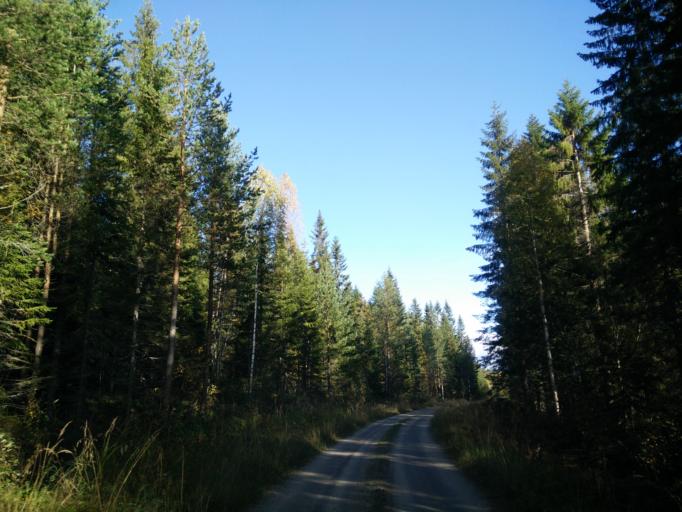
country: SE
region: Vaesternorrland
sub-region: Sundsvalls Kommun
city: Matfors
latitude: 62.3364
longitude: 16.8741
